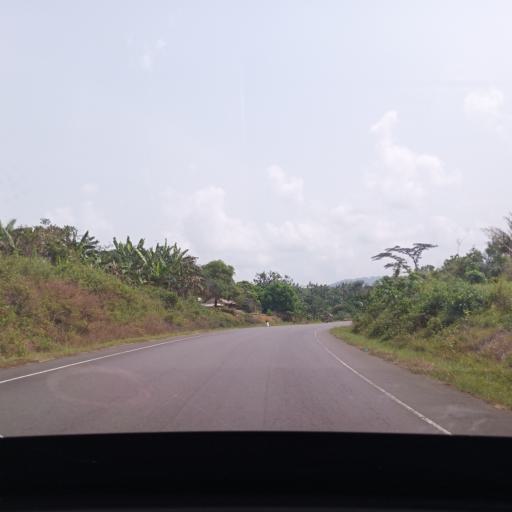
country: LR
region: Margibi
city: Kakata
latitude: 6.2528
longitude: -10.3029
